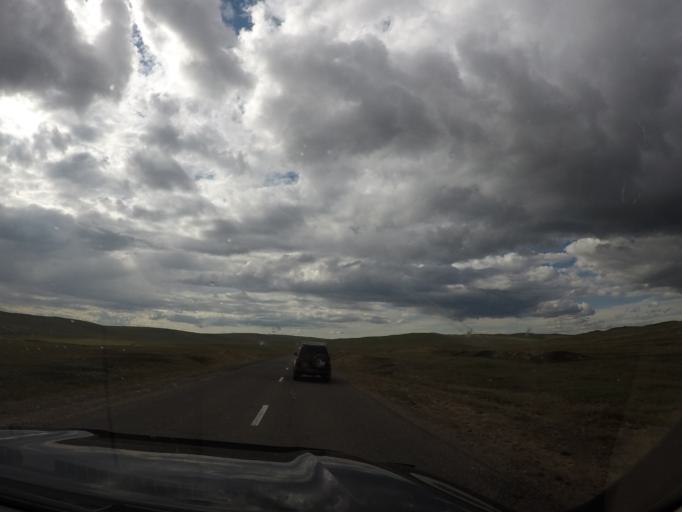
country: MN
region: Hentiy
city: Modot
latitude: 47.5573
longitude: 109.3429
